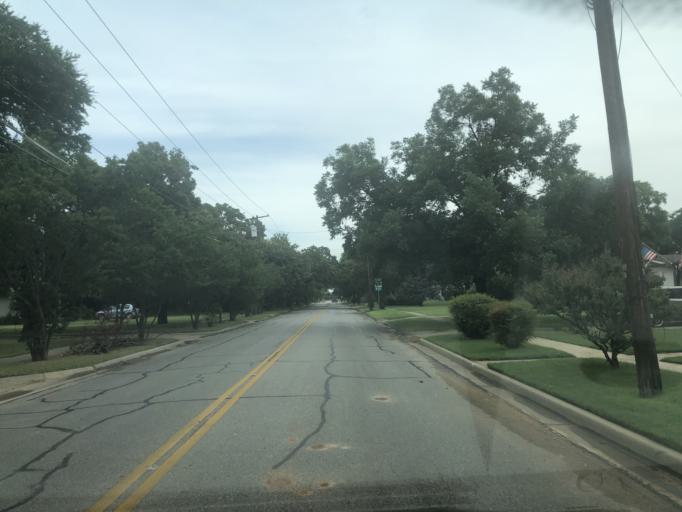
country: US
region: Texas
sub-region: Dallas County
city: Irving
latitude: 32.8097
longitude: -96.9499
